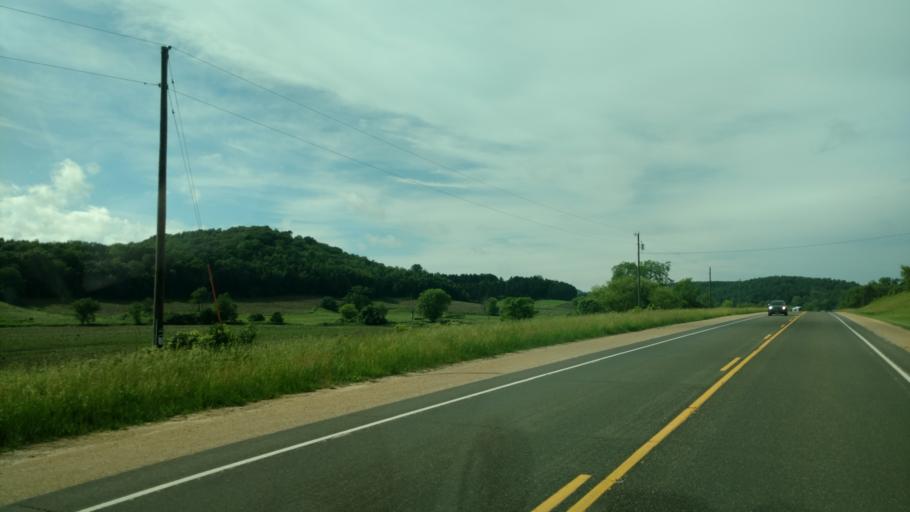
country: US
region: Wisconsin
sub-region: Monroe County
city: Tomah
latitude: 43.8583
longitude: -90.4738
